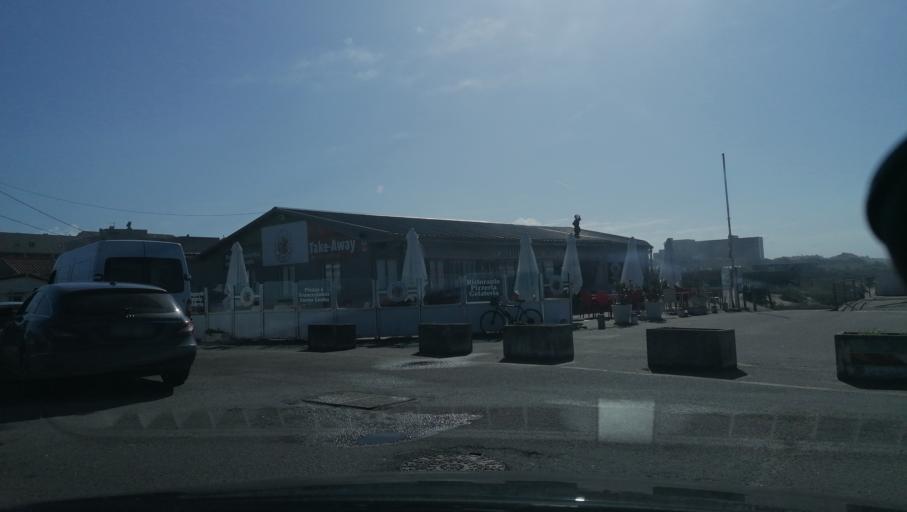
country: PT
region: Porto
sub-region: Vila Nova de Gaia
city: Arcozelo
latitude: 41.0340
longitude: -8.6467
